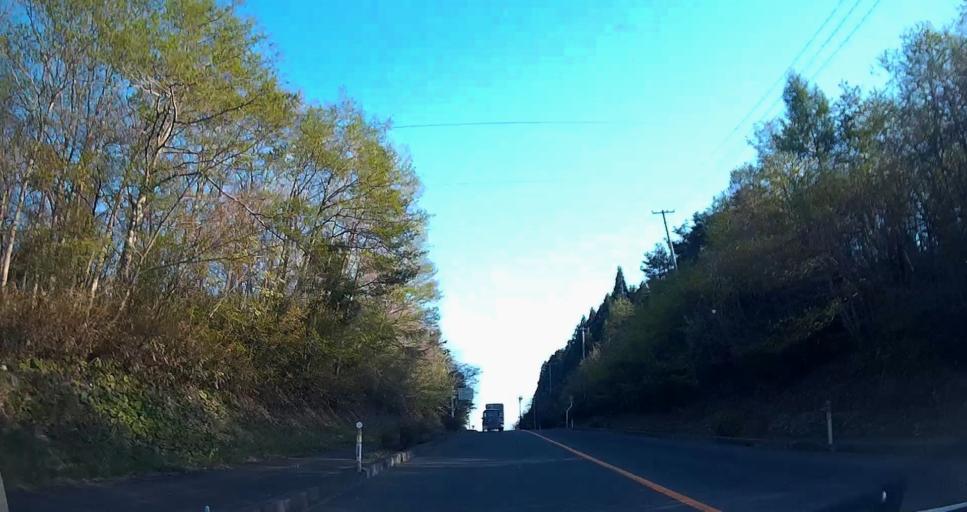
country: JP
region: Aomori
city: Mutsu
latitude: 41.3141
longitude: 141.2155
